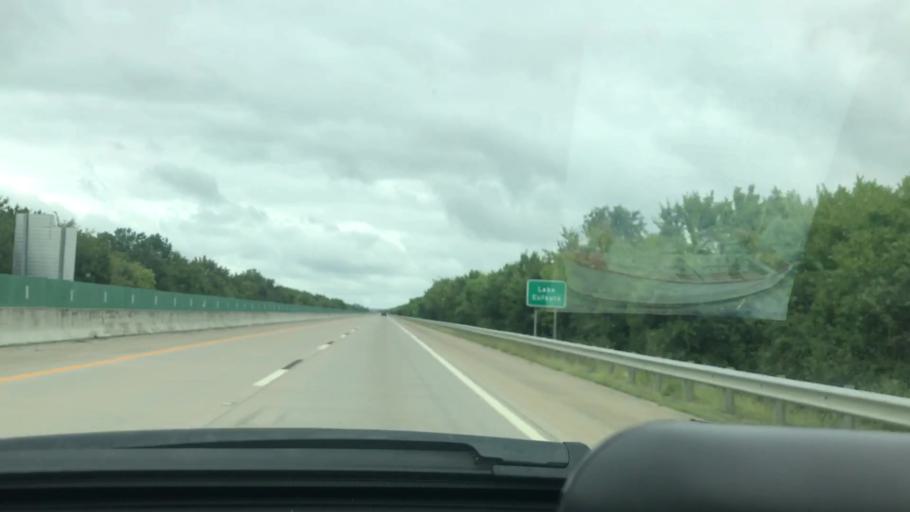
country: US
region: Oklahoma
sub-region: Pittsburg County
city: Krebs
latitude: 35.0166
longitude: -95.7182
